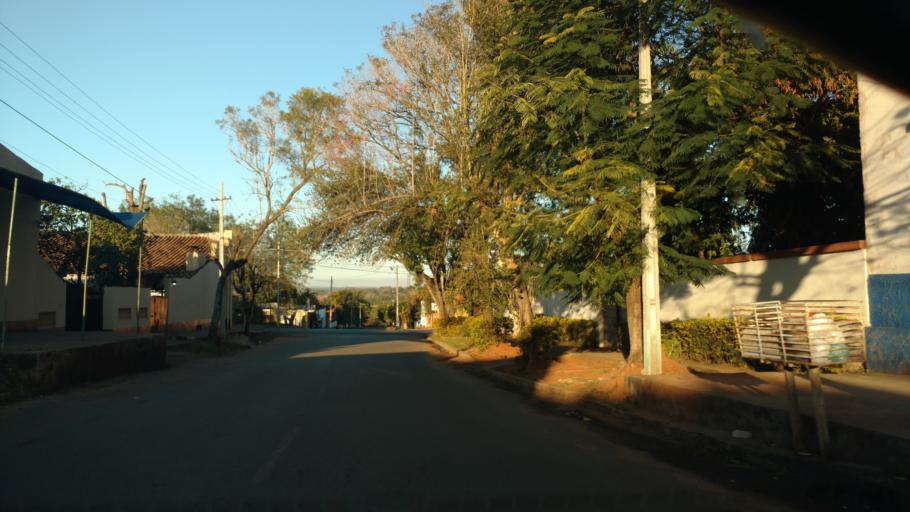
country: PY
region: Paraguari
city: Yaguaron
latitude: -25.5666
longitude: -57.2841
